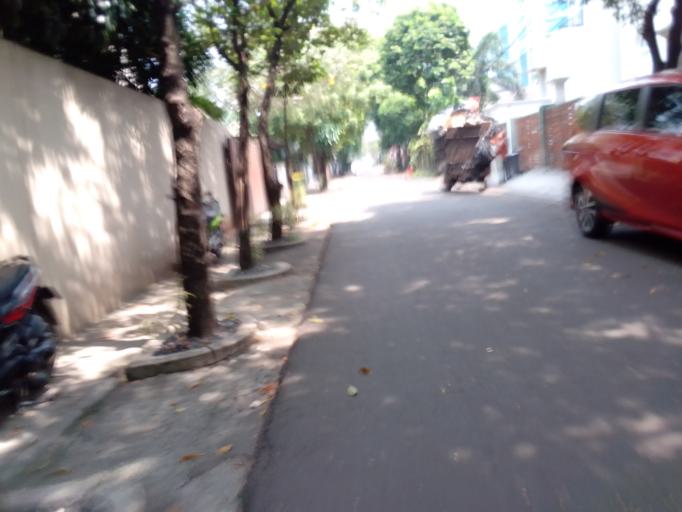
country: ID
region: Jakarta Raya
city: Jakarta
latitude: -6.2297
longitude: 106.8123
